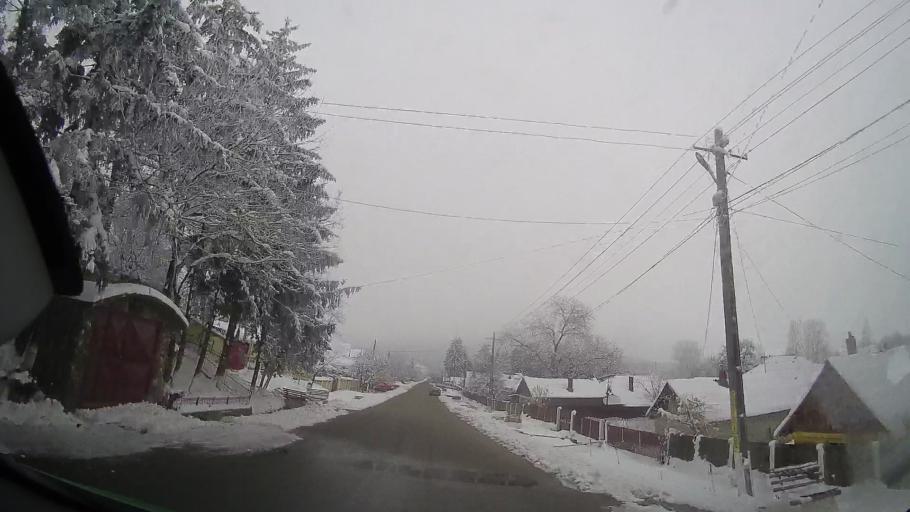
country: RO
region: Neamt
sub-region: Comuna Valea Ursului
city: Valea Ursului
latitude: 46.8530
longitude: 27.0529
